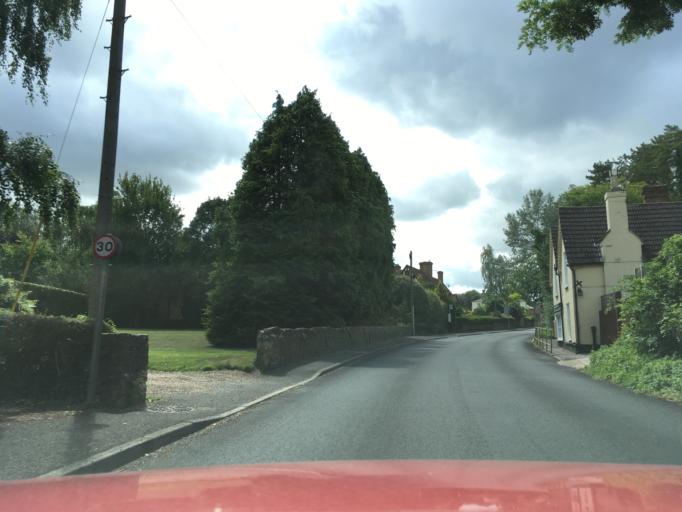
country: GB
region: England
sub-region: Kent
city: West Malling
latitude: 51.2873
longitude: 0.4024
